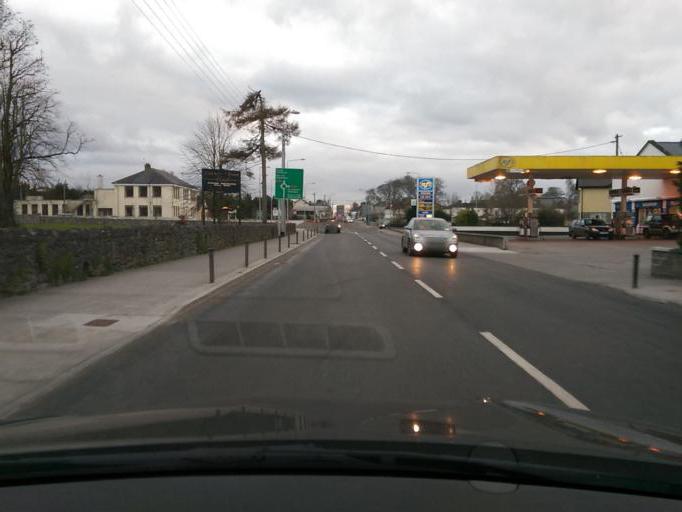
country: IE
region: Leinster
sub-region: Uibh Fhaili
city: Birr
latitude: 53.0906
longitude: -7.9076
